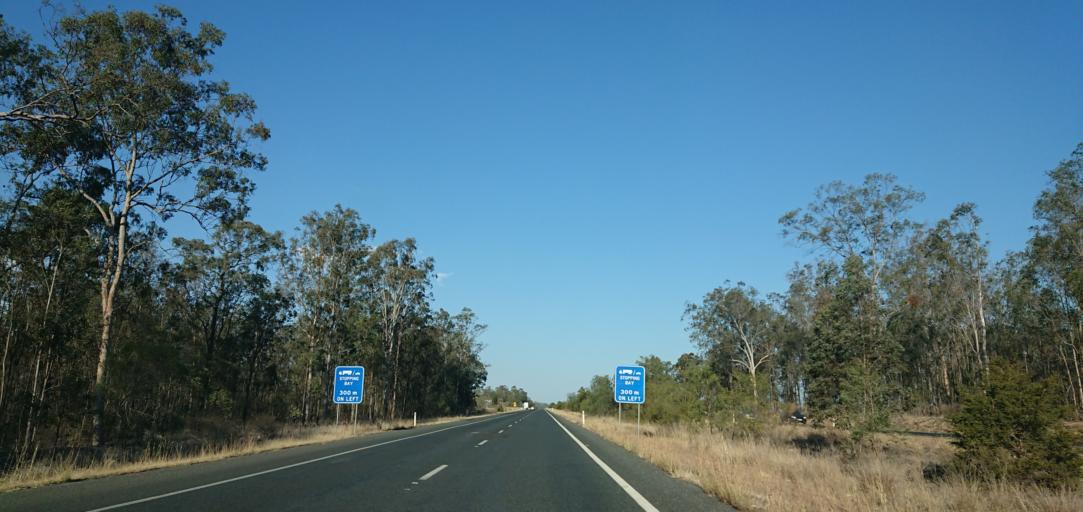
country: AU
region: Queensland
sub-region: Lockyer Valley
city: Gatton
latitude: -27.5514
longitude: 152.1478
